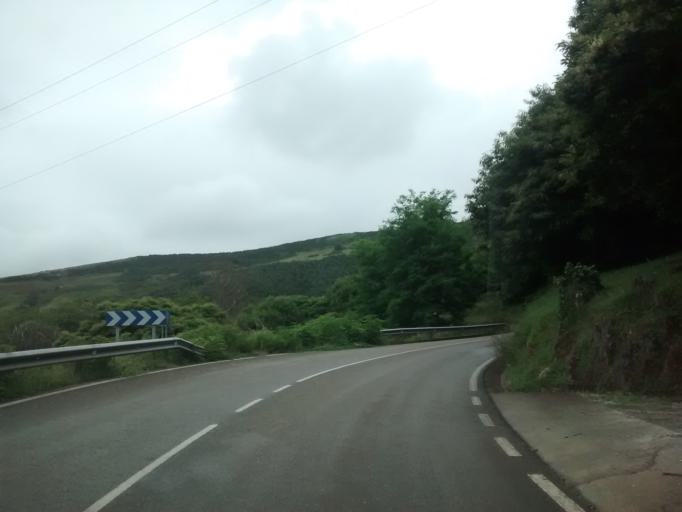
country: ES
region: Cantabria
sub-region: Provincia de Cantabria
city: Santillana
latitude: 43.4111
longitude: -4.1007
